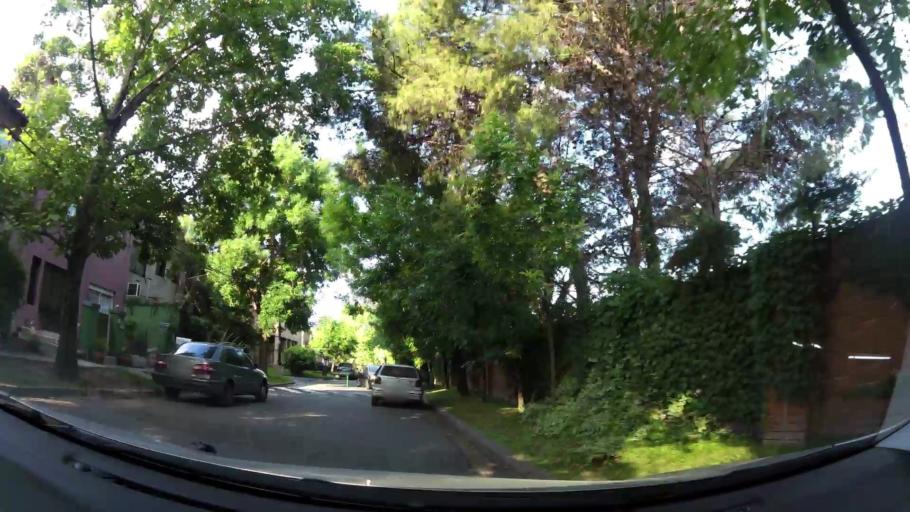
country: AR
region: Buenos Aires
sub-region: Partido de Tigre
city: Tigre
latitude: -34.4714
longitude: -58.5633
